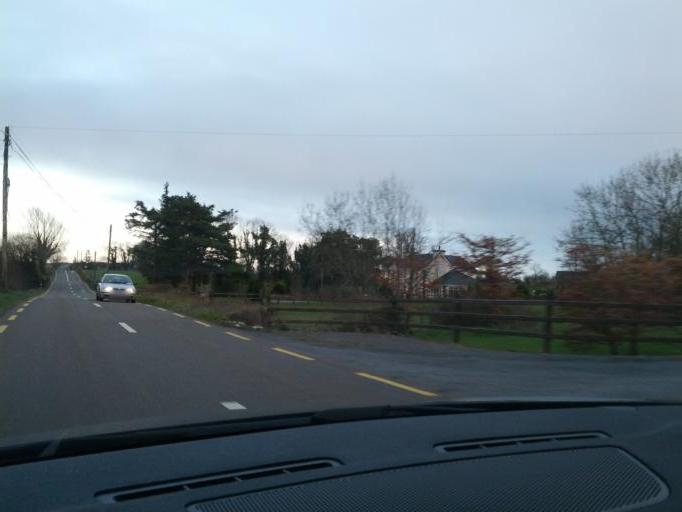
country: IE
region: Connaught
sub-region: Sligo
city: Ballymote
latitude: 53.9876
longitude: -8.4883
